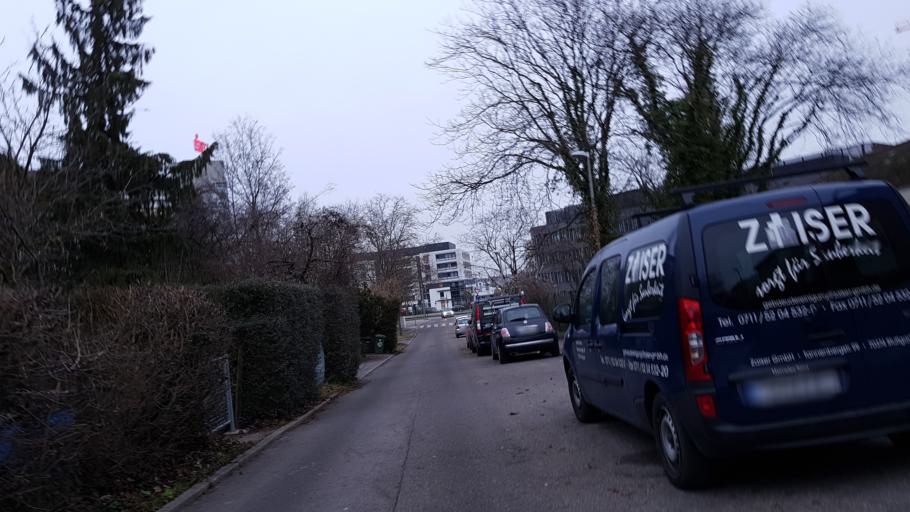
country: DE
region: Baden-Wuerttemberg
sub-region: Regierungsbezirk Stuttgart
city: Stuttgart
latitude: 48.8088
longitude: 9.1889
